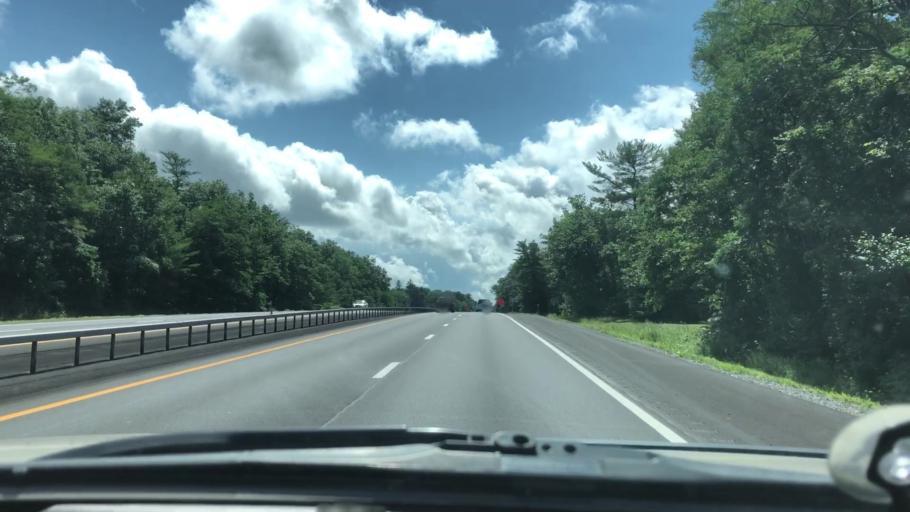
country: US
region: New York
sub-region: Greene County
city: Cairo
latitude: 42.3046
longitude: -73.9990
